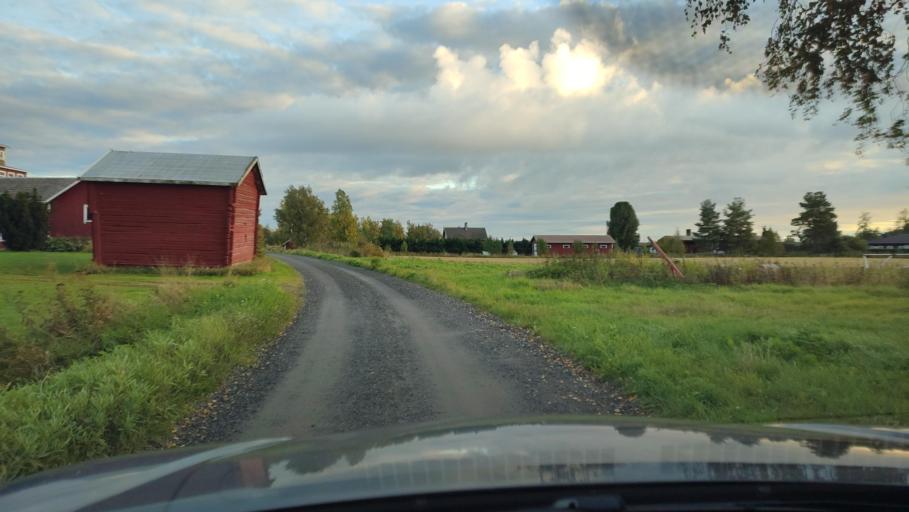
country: FI
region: Ostrobothnia
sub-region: Sydosterbotten
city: Kristinestad
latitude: 62.2501
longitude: 21.5114
